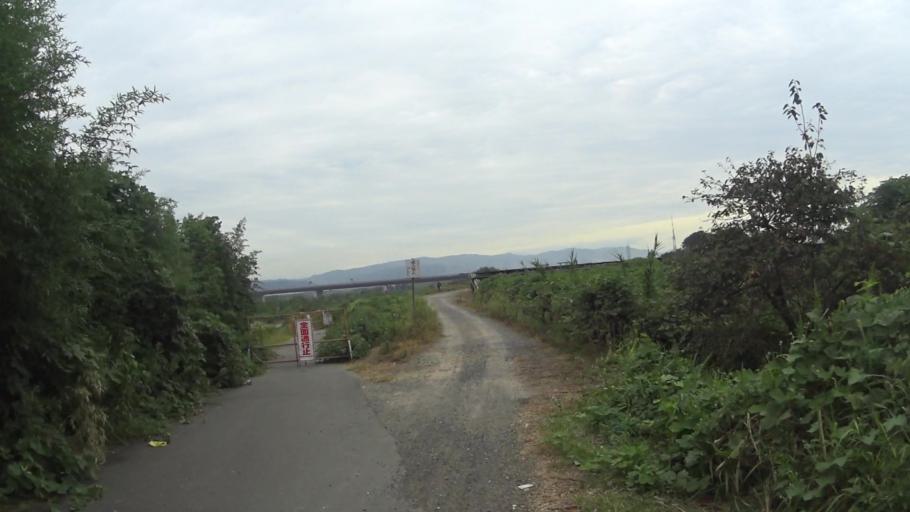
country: JP
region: Kyoto
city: Yawata
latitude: 34.8691
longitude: 135.7497
